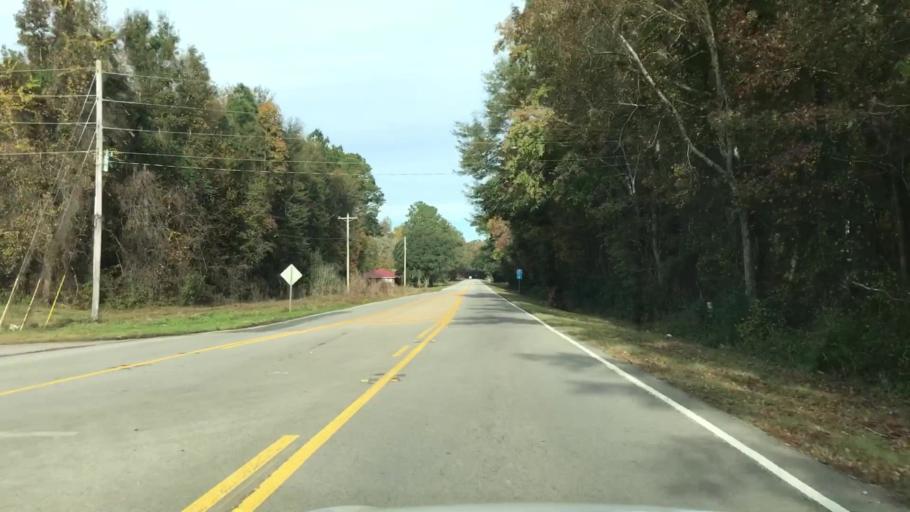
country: US
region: South Carolina
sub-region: Charleston County
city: Ravenel
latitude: 32.7759
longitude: -80.4621
